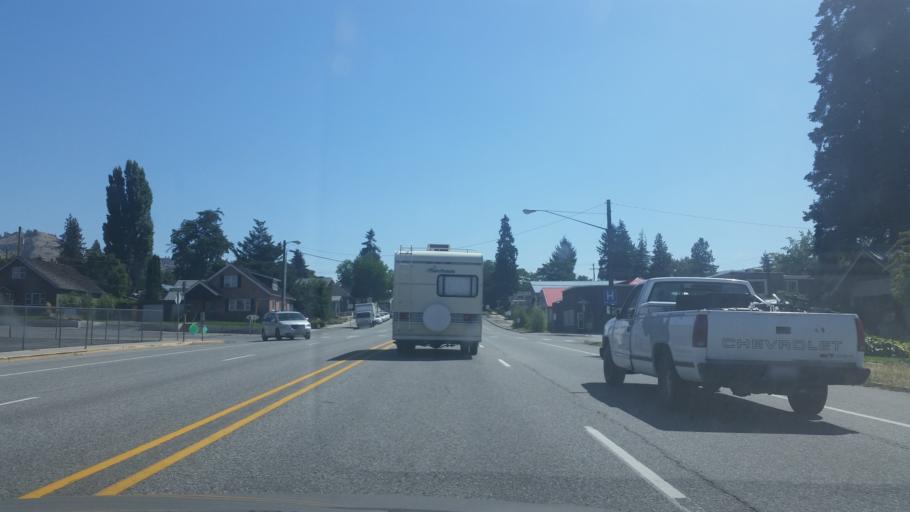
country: US
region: Washington
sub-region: Chelan County
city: Chelan
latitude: 47.8398
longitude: -120.0116
